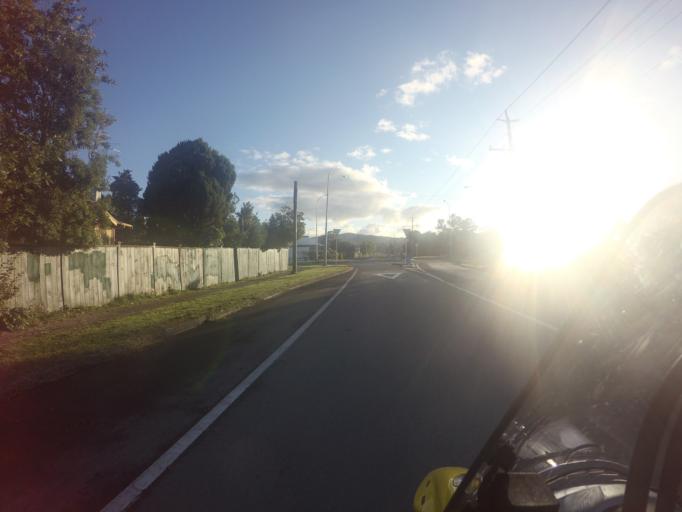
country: NZ
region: Gisborne
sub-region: Gisborne District
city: Gisborne
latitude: -38.6720
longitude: 178.0426
